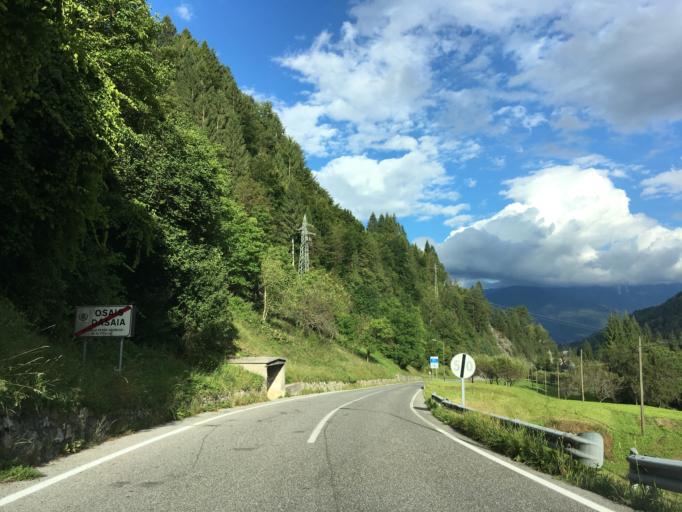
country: IT
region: Friuli Venezia Giulia
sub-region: Provincia di Udine
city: Pieria-Prato Carnico
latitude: 46.5208
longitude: 12.7884
